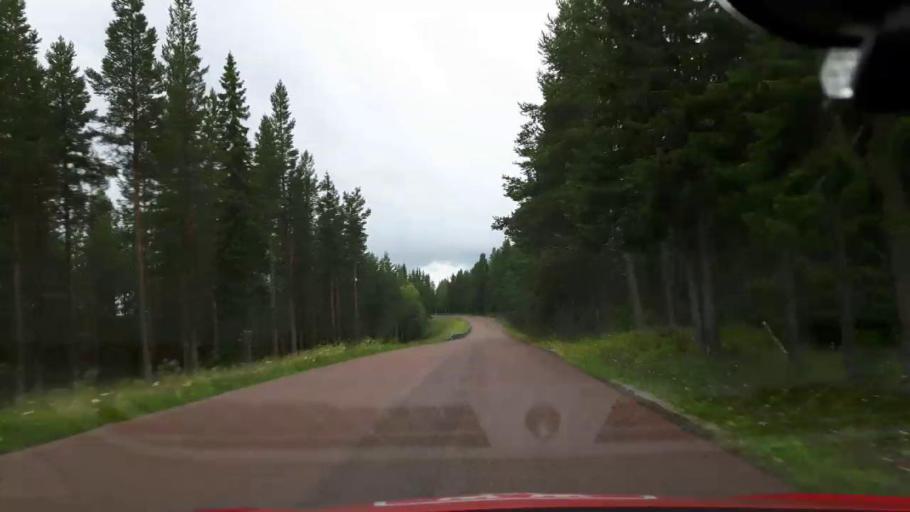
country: SE
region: Jaemtland
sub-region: Krokoms Kommun
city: Valla
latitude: 63.3546
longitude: 13.7264
